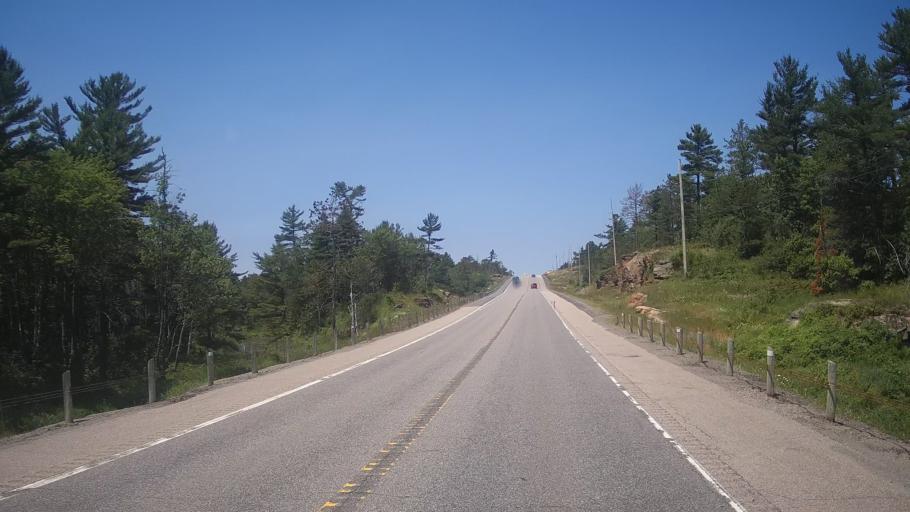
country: CA
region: Ontario
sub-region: Parry Sound District
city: Parry Sound
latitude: 45.6543
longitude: -80.4071
